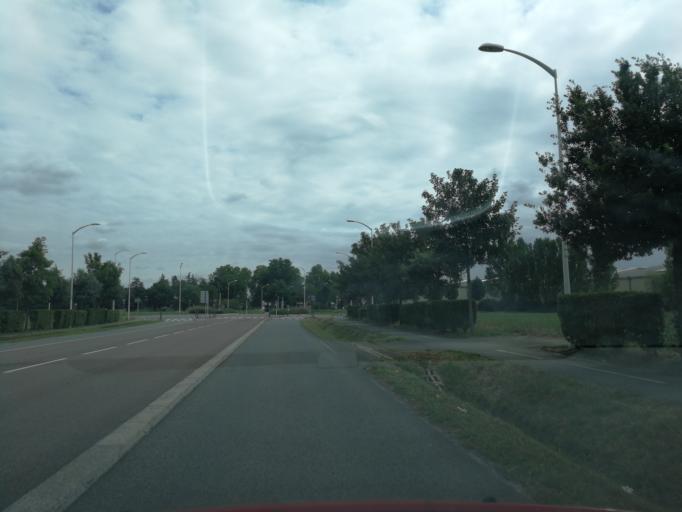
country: FR
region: Midi-Pyrenees
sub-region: Departement de la Haute-Garonne
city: Balma
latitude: 43.5974
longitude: 1.4967
